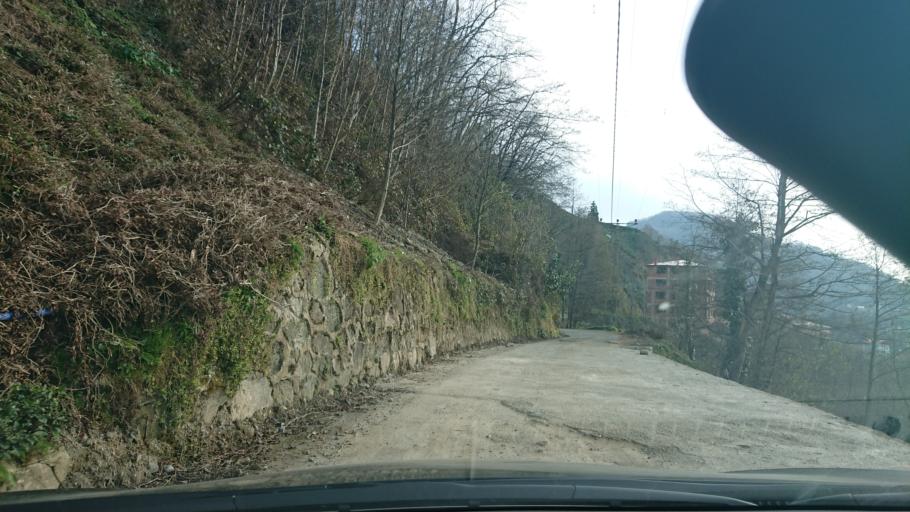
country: TR
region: Rize
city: Rize
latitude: 40.9922
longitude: 40.4928
